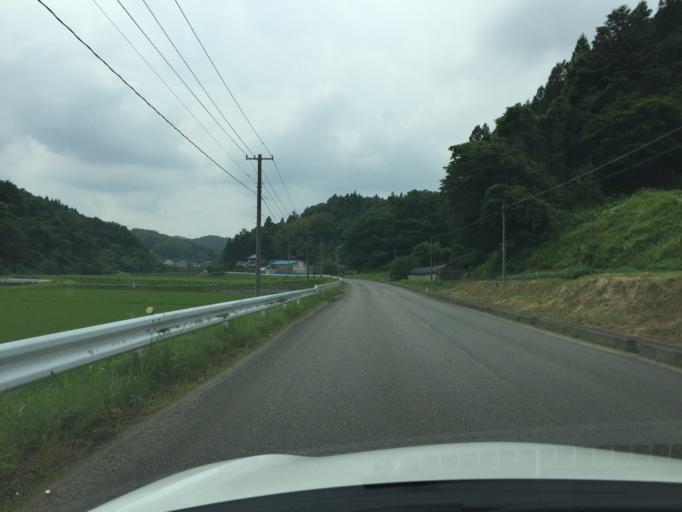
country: JP
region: Fukushima
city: Funehikimachi-funehiki
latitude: 37.2920
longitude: 140.5857
